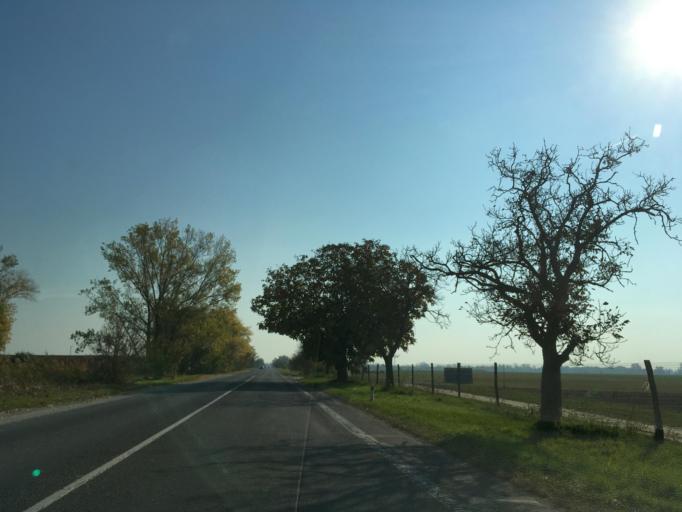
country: SK
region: Trnavsky
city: Samorin
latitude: 48.0562
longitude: 17.2856
